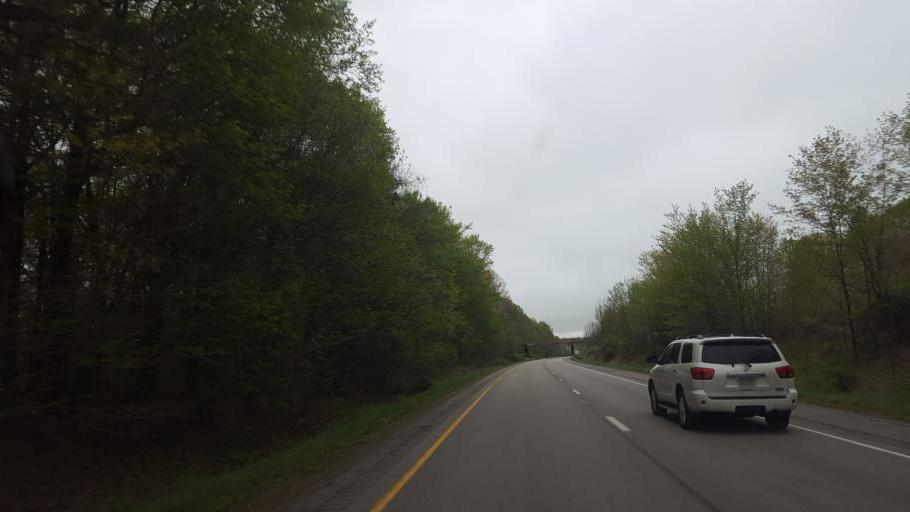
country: US
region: Pennsylvania
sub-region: Mercer County
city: Mercer
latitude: 41.2147
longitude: -80.1636
